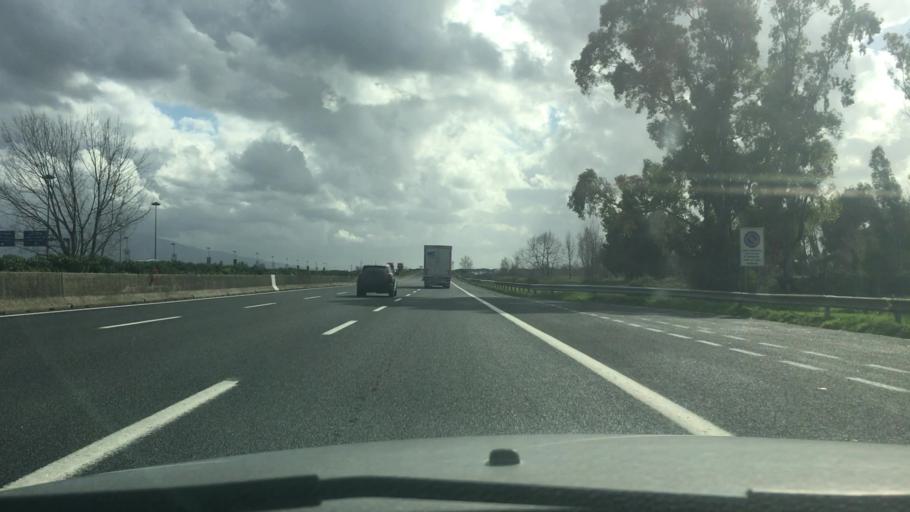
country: IT
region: Campania
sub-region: Provincia di Napoli
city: Pascarola
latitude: 41.0054
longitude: 14.3233
